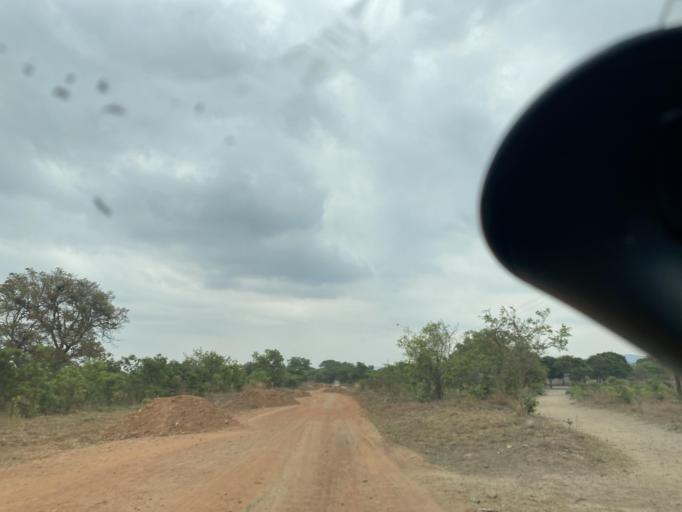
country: ZM
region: Lusaka
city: Chongwe
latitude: -15.2447
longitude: 28.7247
